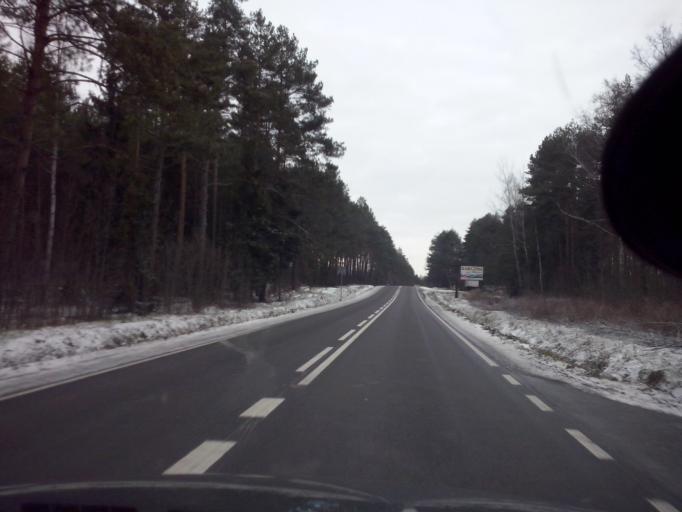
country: PL
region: Lublin Voivodeship
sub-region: Powiat bilgorajski
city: Bilgoraj
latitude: 50.5630
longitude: 22.7759
